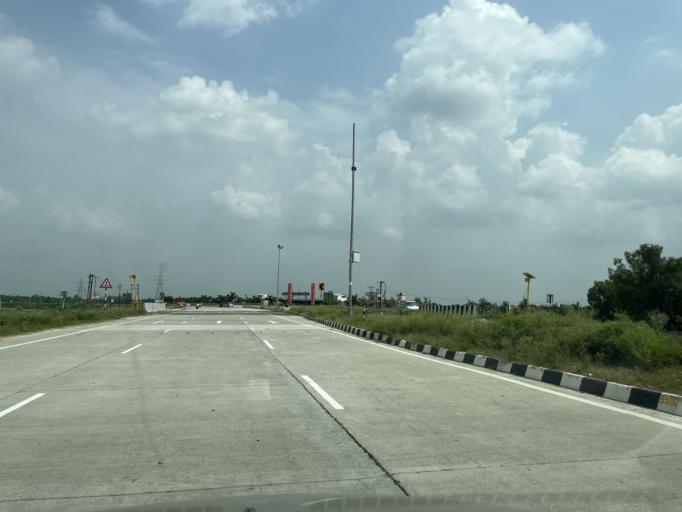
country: IN
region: Uttar Pradesh
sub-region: Bijnor
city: Dhampur
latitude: 29.3170
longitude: 78.5363
